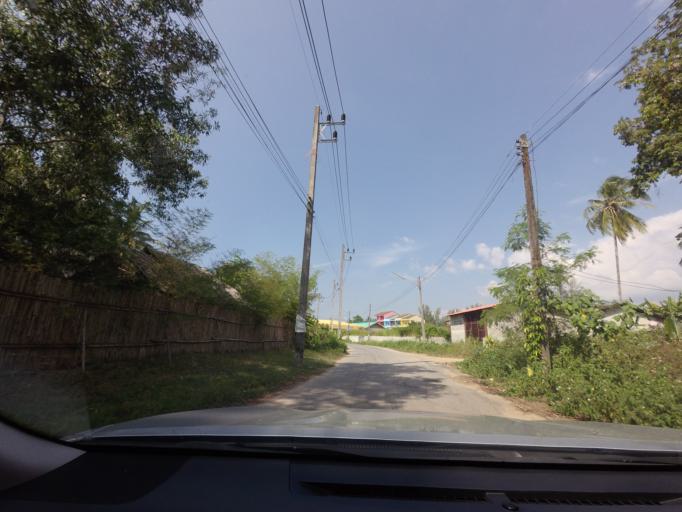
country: TH
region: Phangnga
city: Ban Khao Lak
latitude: 8.6659
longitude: 98.2492
